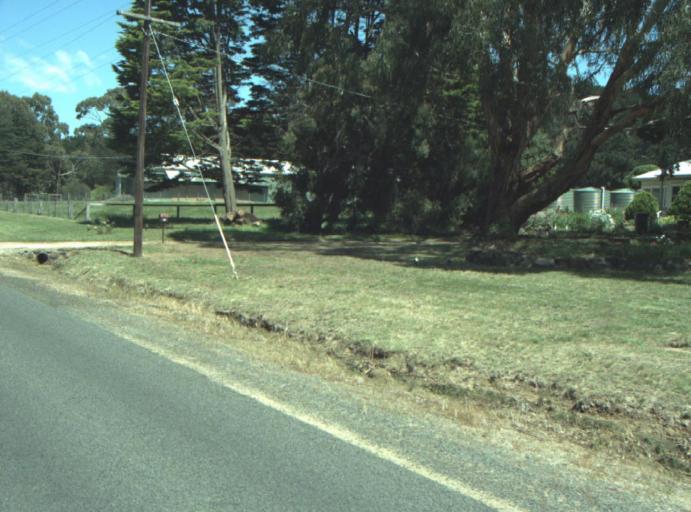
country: AU
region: Victoria
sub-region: Greater Geelong
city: Lara
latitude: -37.8805
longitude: 144.2635
